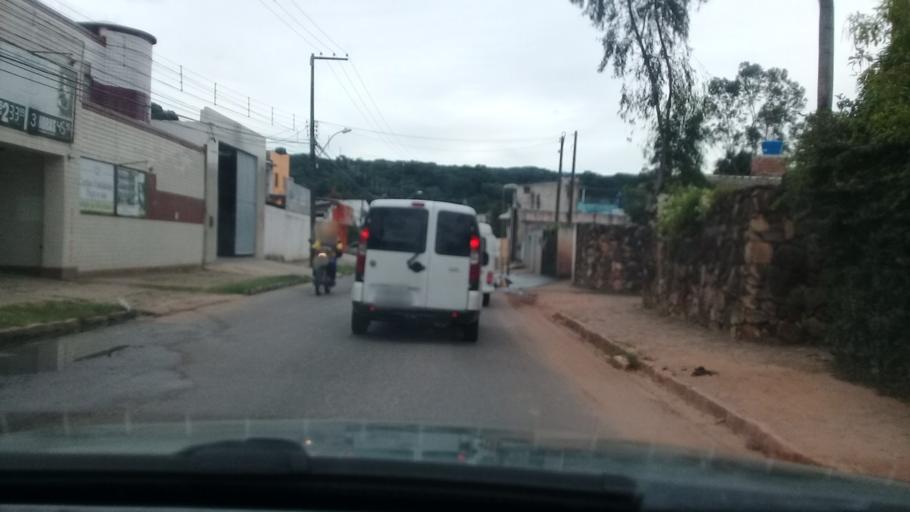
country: BR
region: Pernambuco
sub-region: Sao Lourenco Da Mata
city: Sao Lourenco da Mata
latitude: -8.0364
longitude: -34.9626
